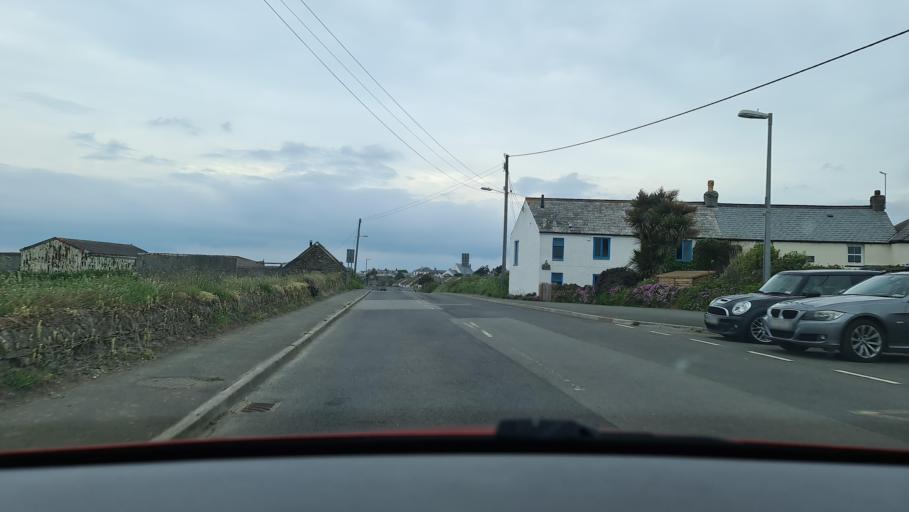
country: GB
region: England
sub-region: Cornwall
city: Tintagel
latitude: 50.6581
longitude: -4.7488
